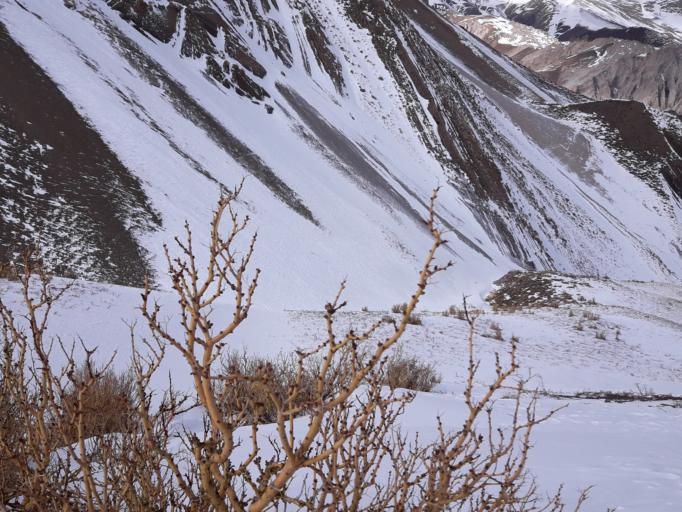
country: AR
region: Mendoza
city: Malargue
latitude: -35.0953
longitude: -70.0861
